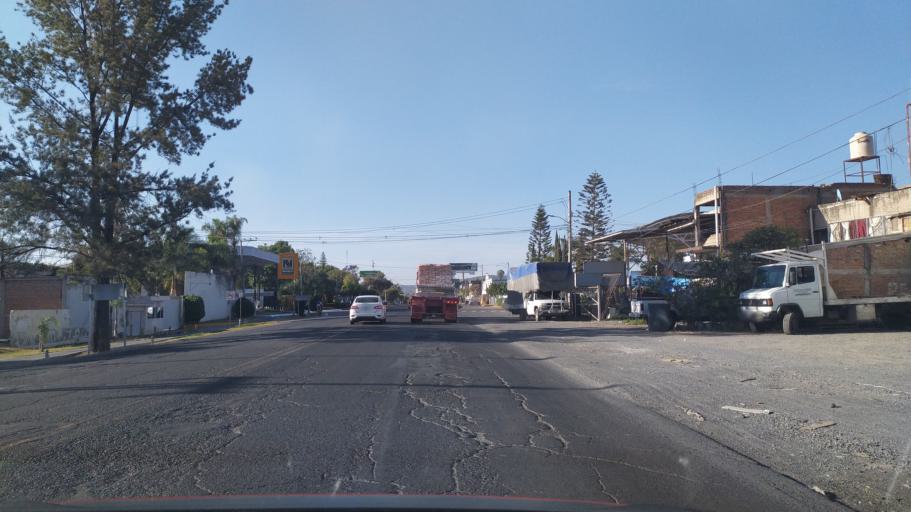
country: MX
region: Jalisco
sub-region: Poncitlan
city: Cuitzeo (La Estancia)
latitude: 20.3318
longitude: -102.7747
